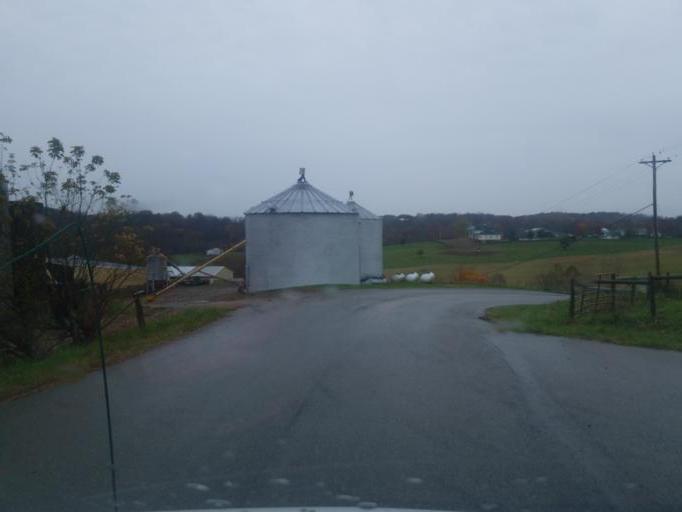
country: US
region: West Virginia
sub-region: Wood County
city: Vienna
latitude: 39.4250
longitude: -81.6194
